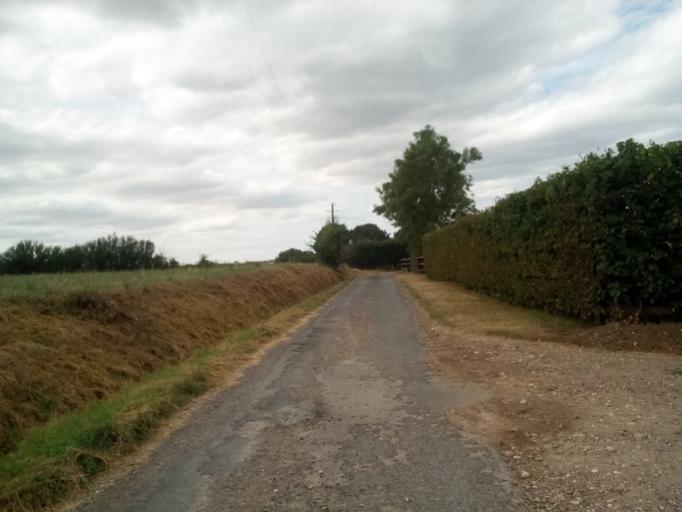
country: FR
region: Lower Normandy
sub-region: Departement du Calvados
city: Troarn
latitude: 49.1693
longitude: -0.1649
